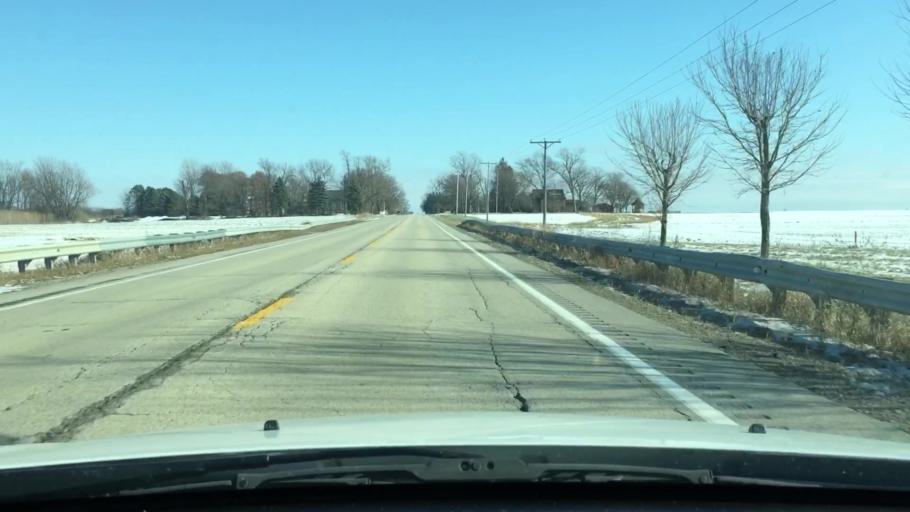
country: US
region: Illinois
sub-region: DeKalb County
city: Malta
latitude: 42.0014
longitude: -88.8187
